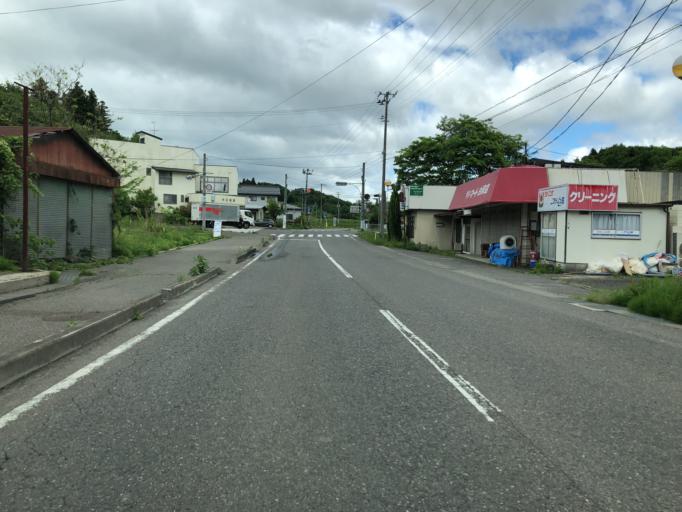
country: JP
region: Fukushima
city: Motomiya
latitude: 37.5000
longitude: 140.4666
